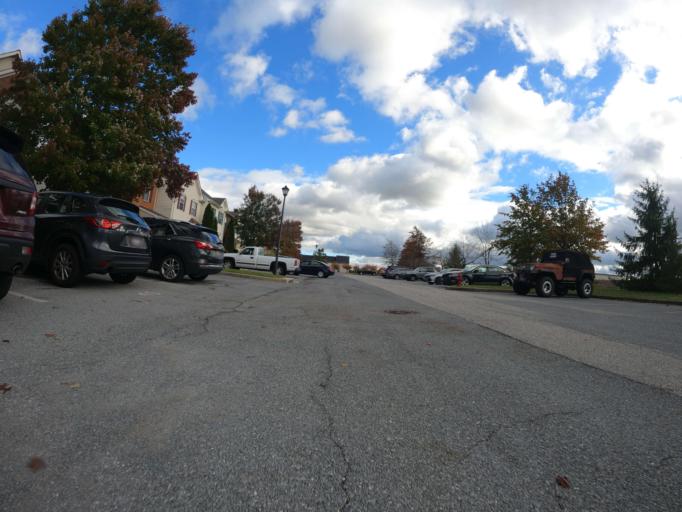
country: US
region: Maryland
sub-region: Carroll County
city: Mount Airy
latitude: 39.3682
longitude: -77.1349
